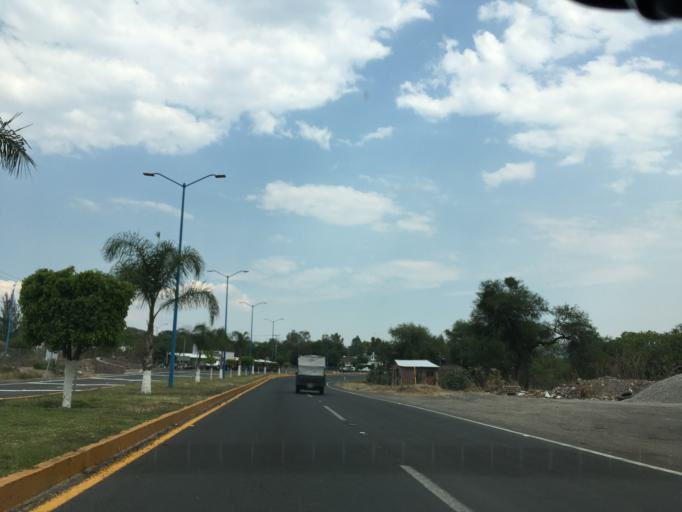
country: MX
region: Michoacan
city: Cuitzeo del Porvenir
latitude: 19.9629
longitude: -101.1389
